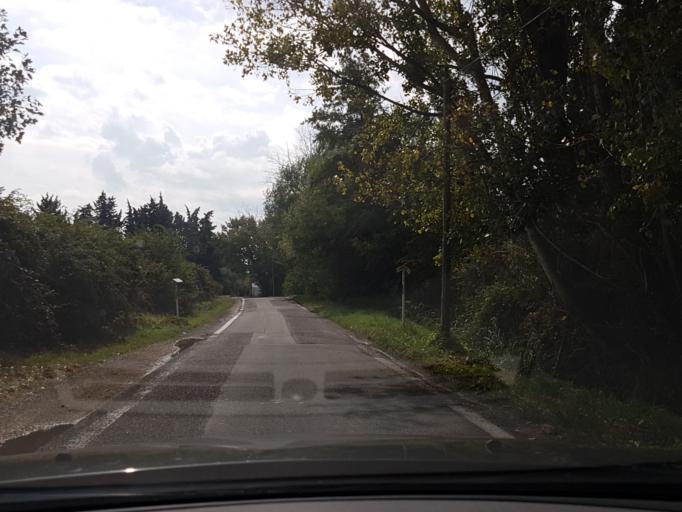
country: FR
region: Provence-Alpes-Cote d'Azur
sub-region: Departement du Vaucluse
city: Saint-Saturnin-les-Avignon
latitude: 43.9636
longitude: 4.9406
